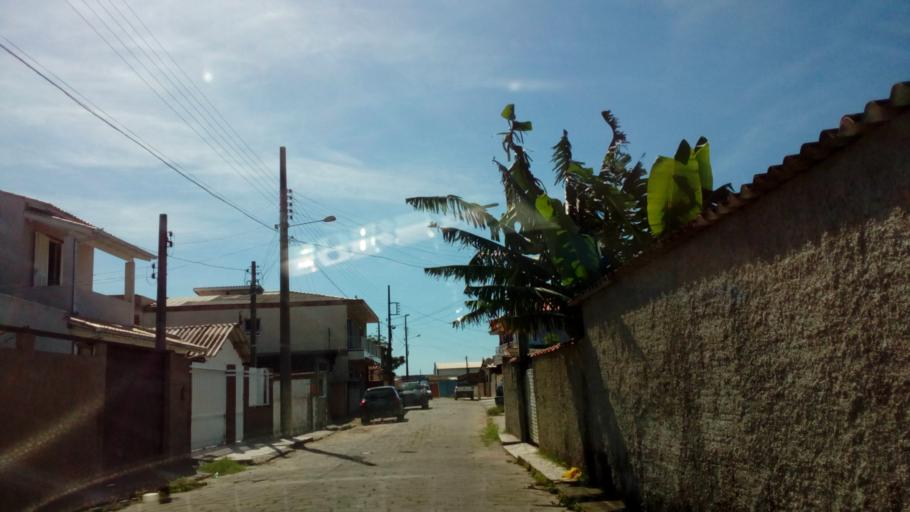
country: BR
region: Santa Catarina
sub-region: Laguna
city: Laguna
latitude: -28.4963
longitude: -48.7772
